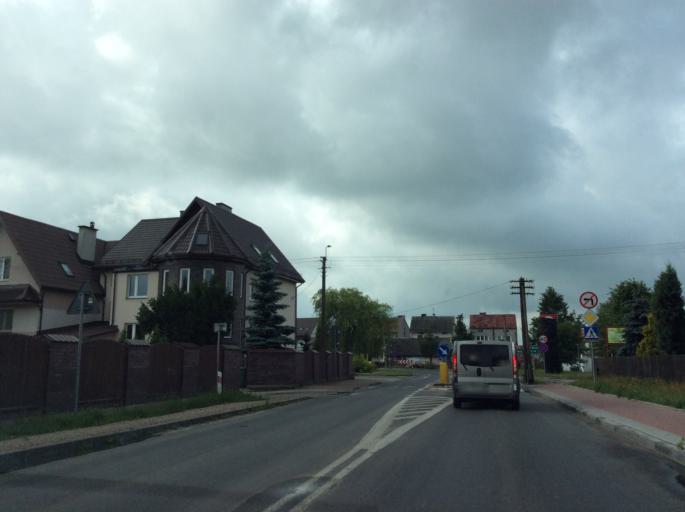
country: PL
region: Masovian Voivodeship
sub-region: Powiat ostrolecki
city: Myszyniec
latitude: 53.3862
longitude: 21.3400
